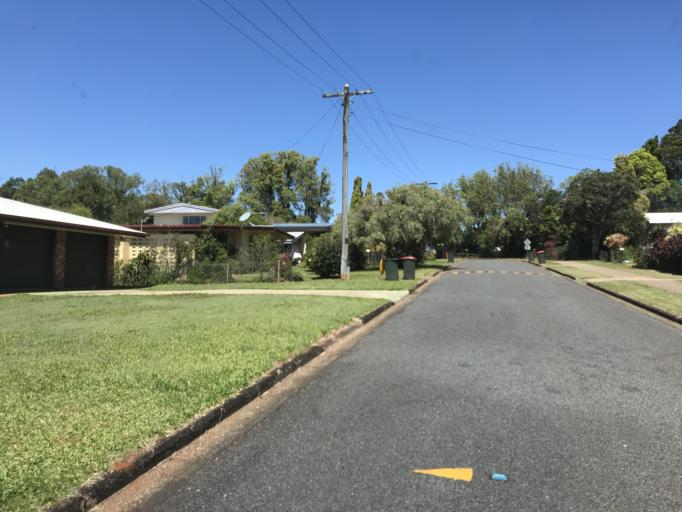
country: AU
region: Queensland
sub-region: Tablelands
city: Atherton
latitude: -17.3553
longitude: 145.5924
